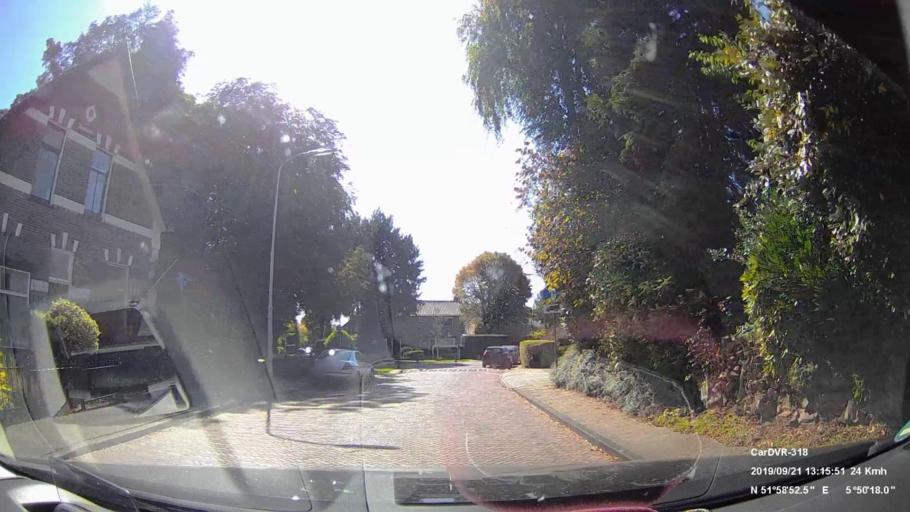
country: NL
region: Gelderland
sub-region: Gemeente Renkum
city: Oosterbeek
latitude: 51.9811
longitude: 5.8383
